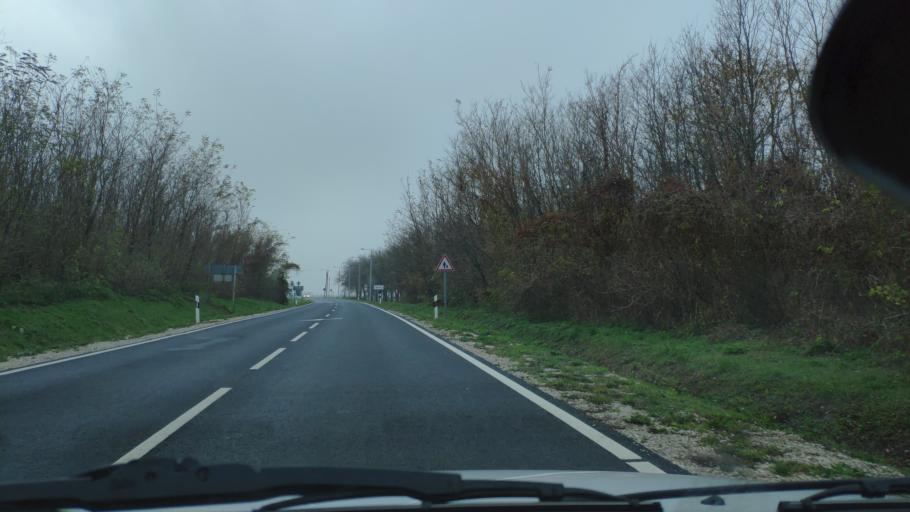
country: HU
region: Zala
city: Zalakomar
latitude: 46.6024
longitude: 17.2661
